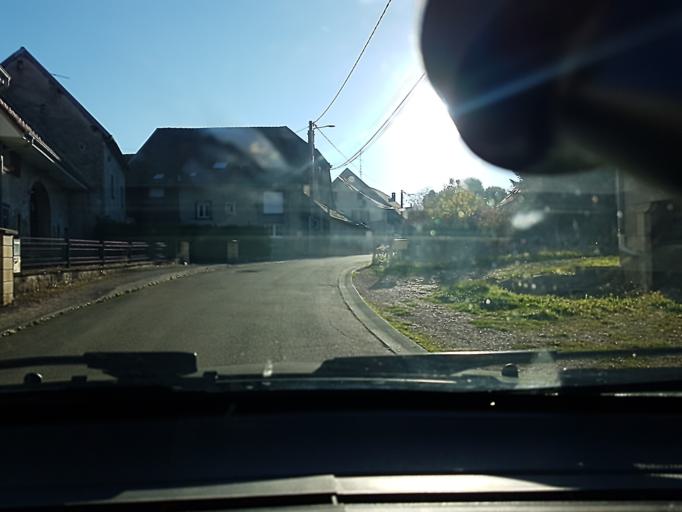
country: FR
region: Franche-Comte
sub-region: Departement du Doubs
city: Herimoncourt
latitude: 47.4314
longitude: 6.9167
